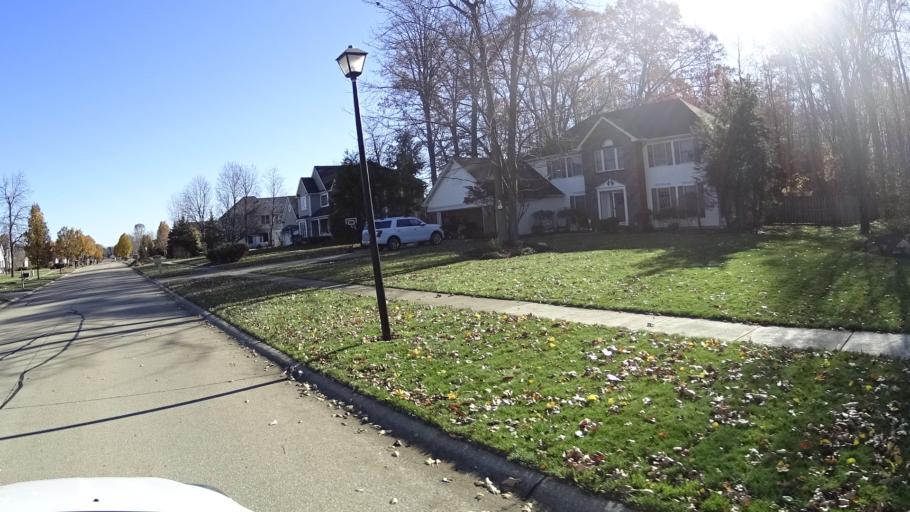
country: US
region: Ohio
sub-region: Lorain County
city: Avon Center
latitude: 41.4397
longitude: -82.0098
